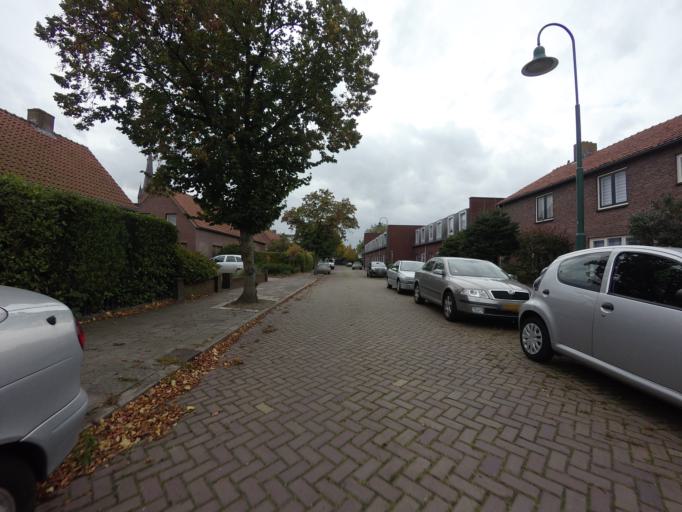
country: NL
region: North Brabant
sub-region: Gemeente Breda
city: Breda
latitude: 51.5530
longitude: 4.7988
